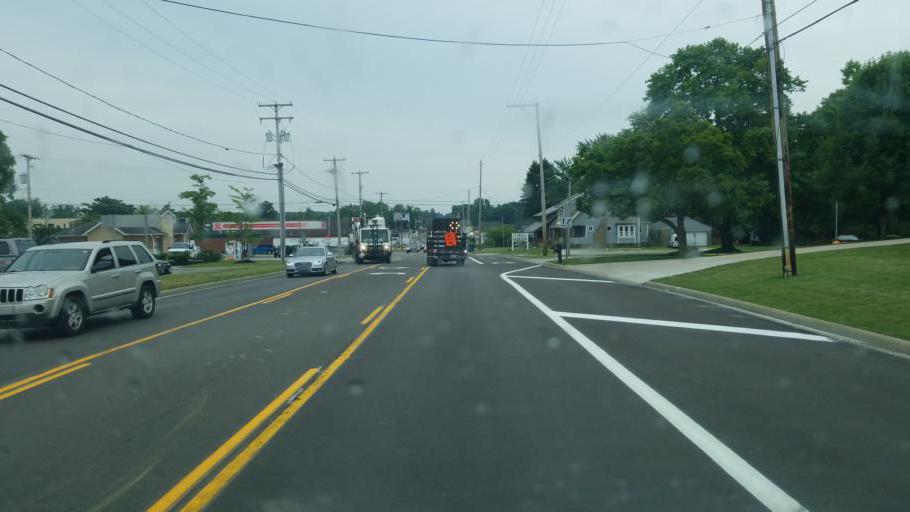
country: US
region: Ohio
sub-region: Summit County
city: Portage Lakes
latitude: 41.0093
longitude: -81.5552
